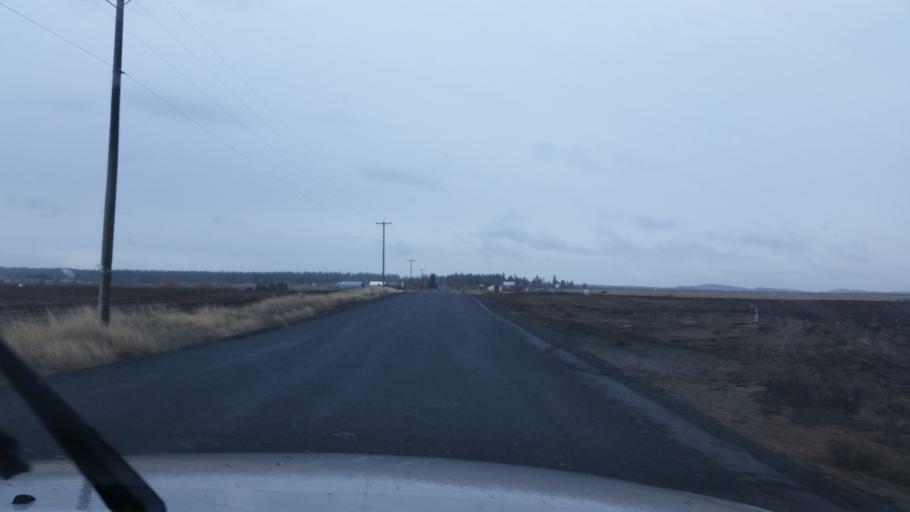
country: US
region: Washington
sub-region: Spokane County
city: Medical Lake
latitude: 47.6144
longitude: -117.7577
